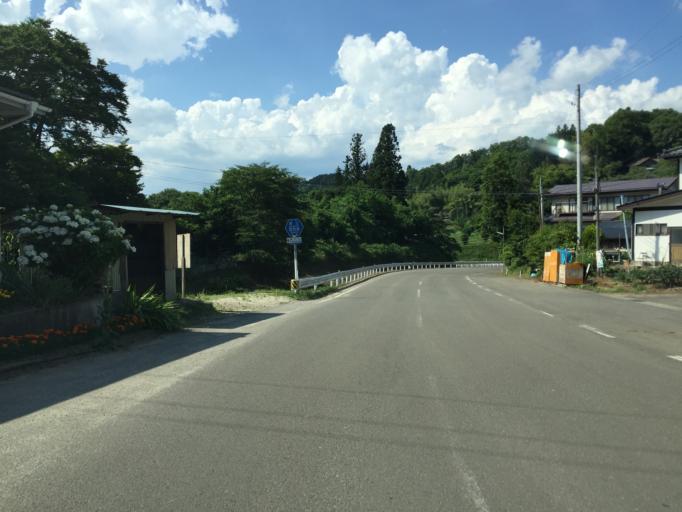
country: JP
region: Fukushima
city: Yanagawamachi-saiwaicho
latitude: 37.7911
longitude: 140.6485
